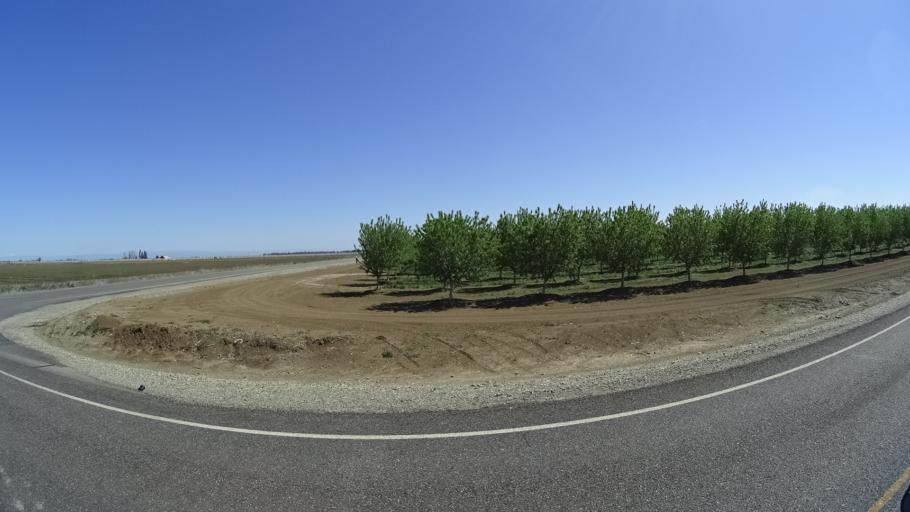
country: US
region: California
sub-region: Glenn County
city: Willows
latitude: 39.5823
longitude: -122.2497
